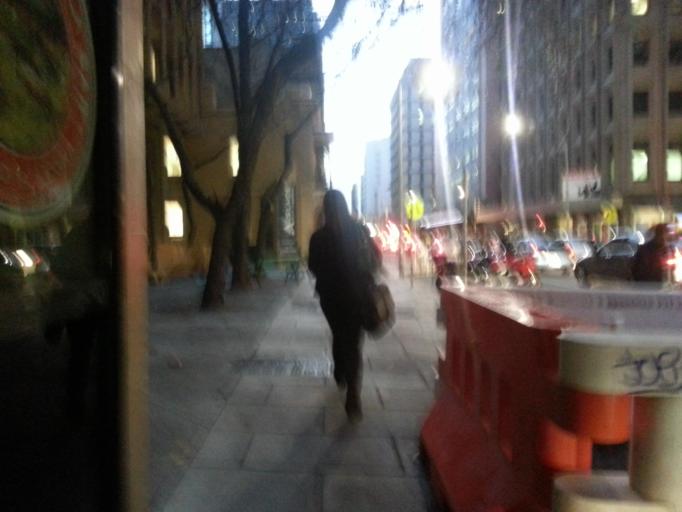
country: AU
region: South Australia
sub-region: Adelaide
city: Adelaide
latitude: -34.9258
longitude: 138.6010
